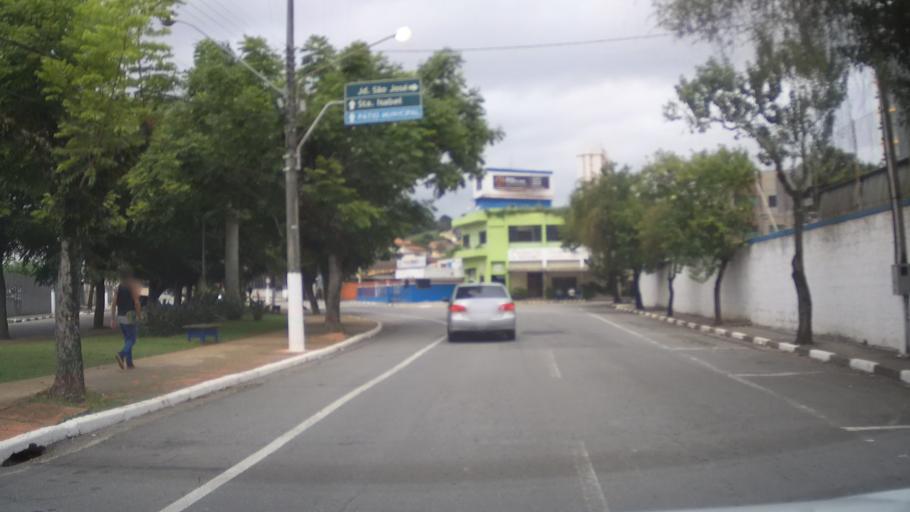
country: BR
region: Sao Paulo
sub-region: Aruja
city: Aruja
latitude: -23.3949
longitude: -46.3163
